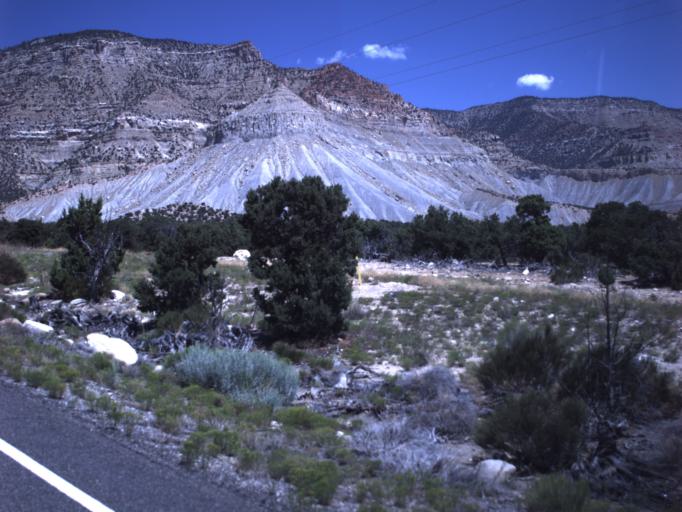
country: US
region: Utah
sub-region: Emery County
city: Orangeville
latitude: 39.2901
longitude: -111.1098
